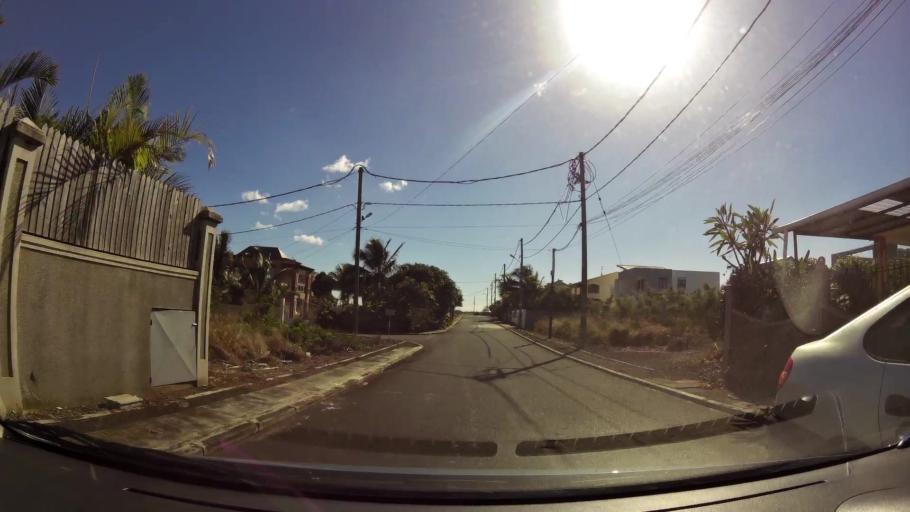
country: MU
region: Black River
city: Flic en Flac
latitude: -20.2782
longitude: 57.3801
